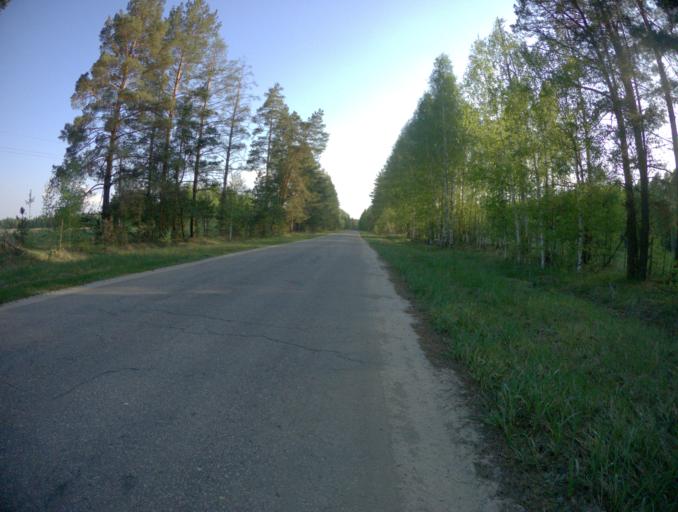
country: RU
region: Vladimir
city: Vyazniki
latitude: 56.3401
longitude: 42.1374
